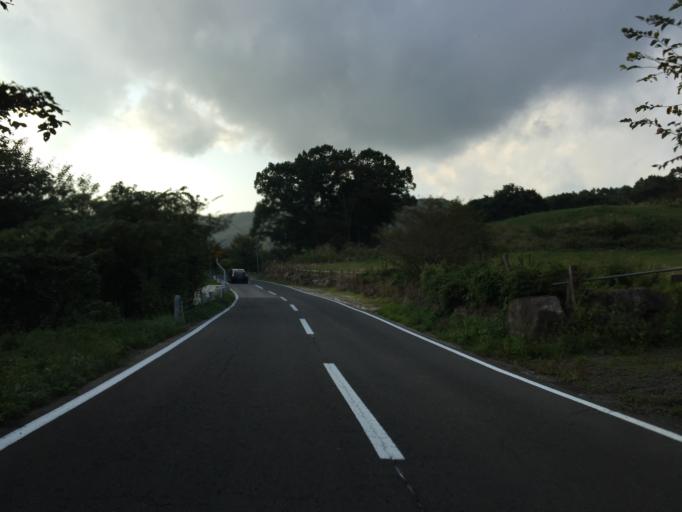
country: JP
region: Fukushima
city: Funehikimachi-funehiki
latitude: 37.5850
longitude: 140.7170
